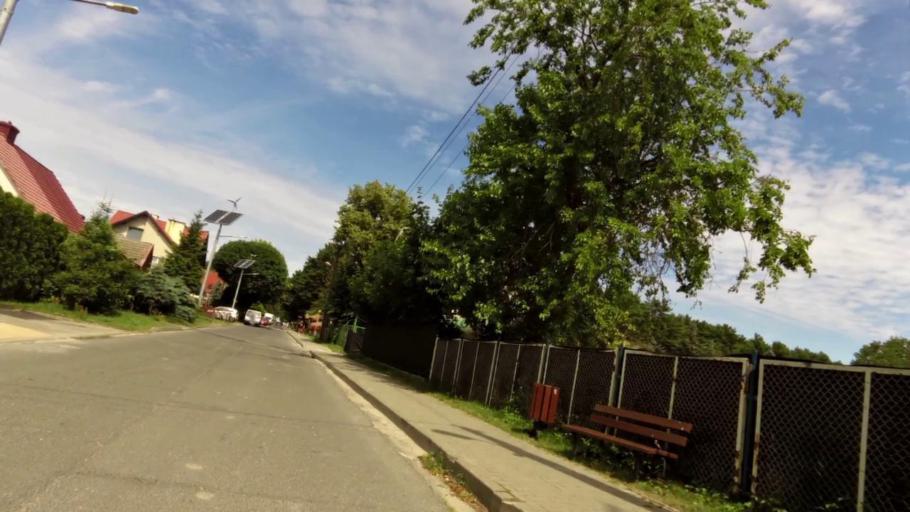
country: PL
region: West Pomeranian Voivodeship
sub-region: Powiat kamienski
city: Dziwnow
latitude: 54.0342
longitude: 14.8089
